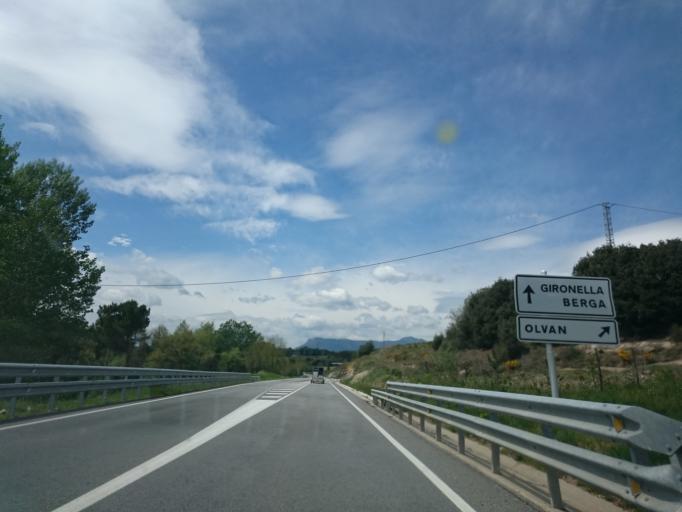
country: ES
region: Catalonia
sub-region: Provincia de Barcelona
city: Olvan
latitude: 42.0509
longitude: 1.9066
